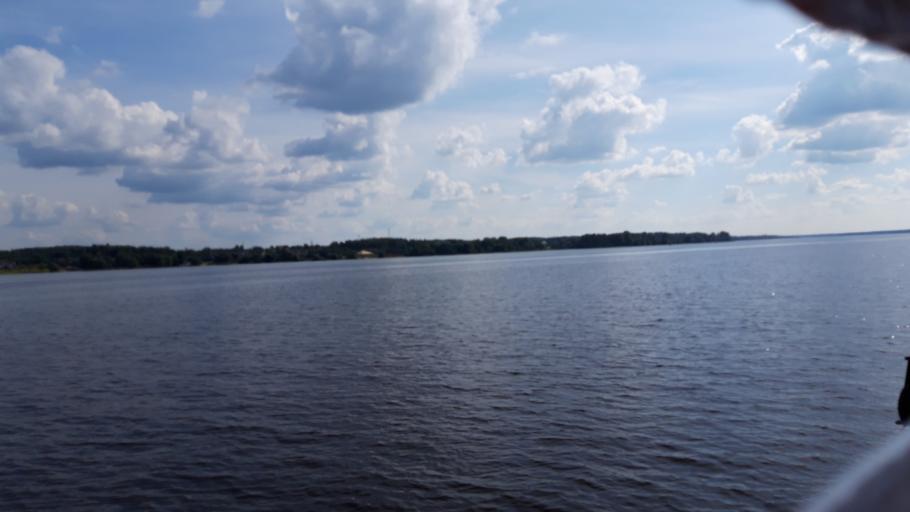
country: RU
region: Tverskaya
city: Konakovo
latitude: 56.6744
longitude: 36.6695
